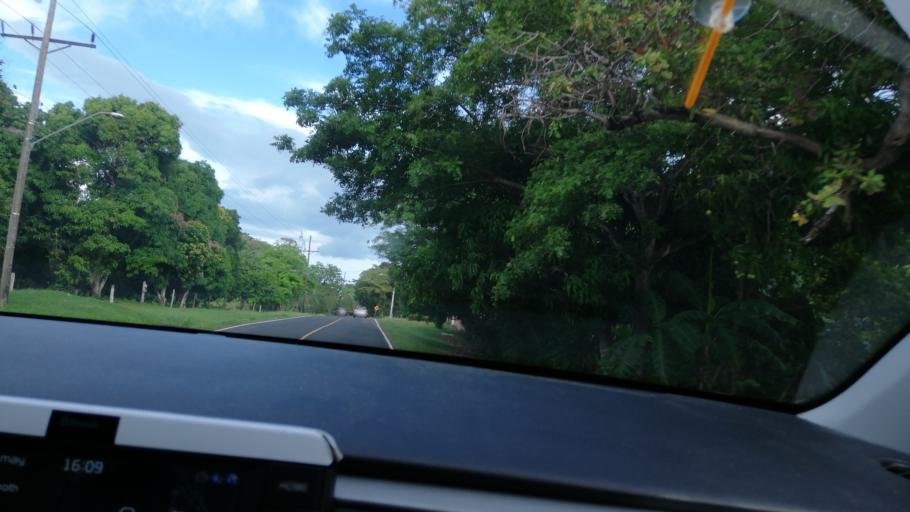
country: PA
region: Panama
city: Las Colinas
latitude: 8.4927
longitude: -80.0250
